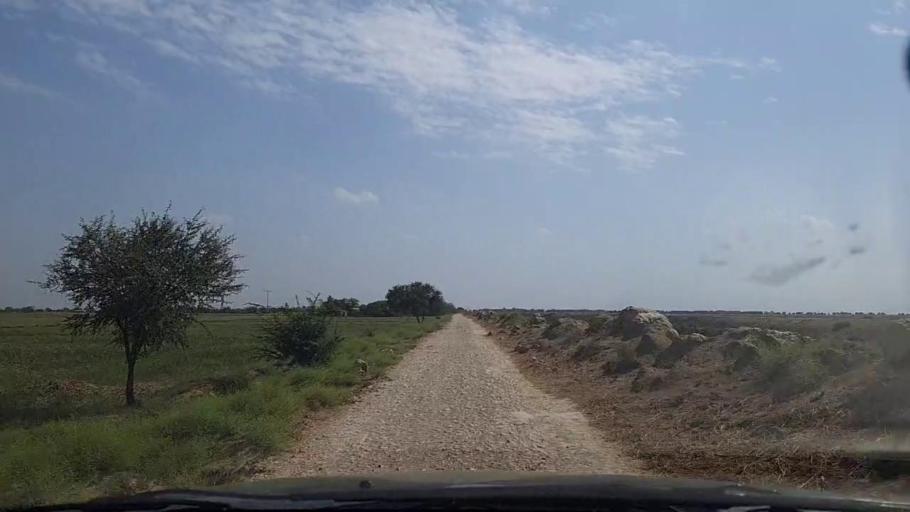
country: PK
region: Sindh
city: Mirpur Batoro
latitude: 24.5769
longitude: 68.1962
